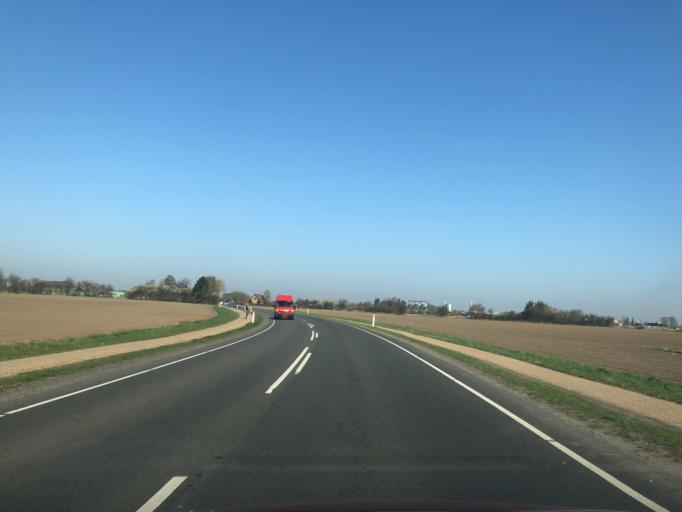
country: DK
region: Zealand
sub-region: Ringsted Kommune
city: Ringsted
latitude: 55.4248
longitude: 11.8219
